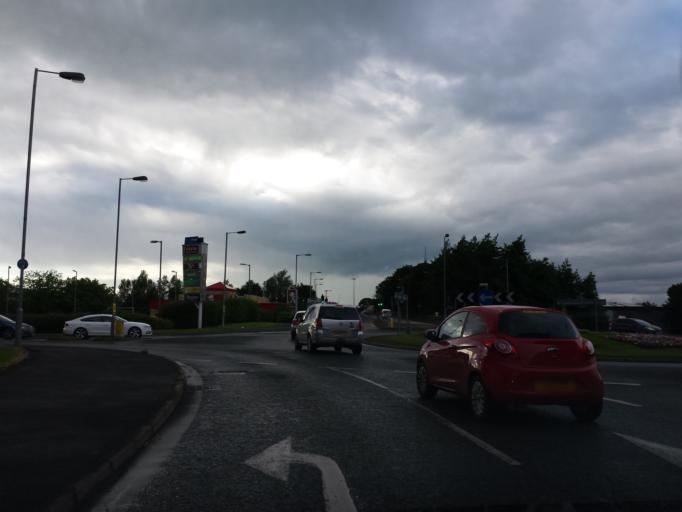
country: GB
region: Scotland
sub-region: Dumfries and Galloway
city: Dumfries
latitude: 55.0760
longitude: -3.6230
